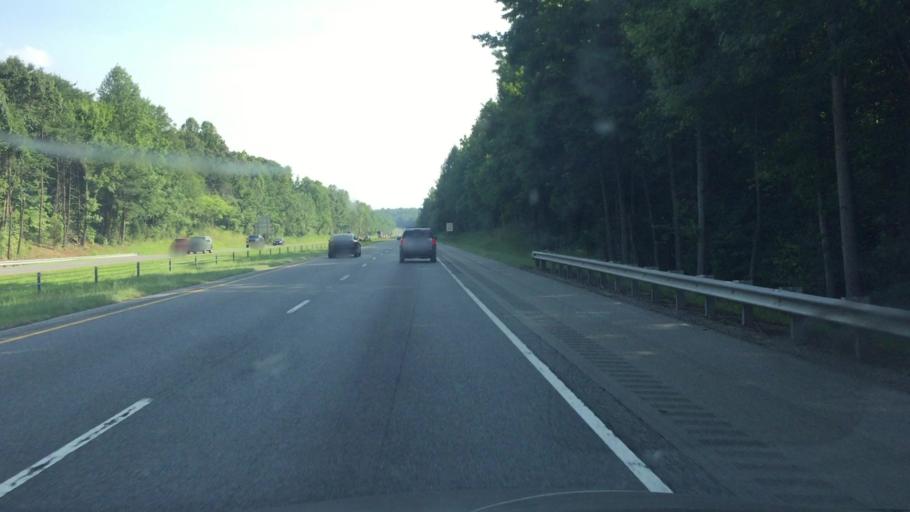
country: US
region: North Carolina
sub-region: Rockingham County
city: Reidsville
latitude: 36.3545
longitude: -79.6310
